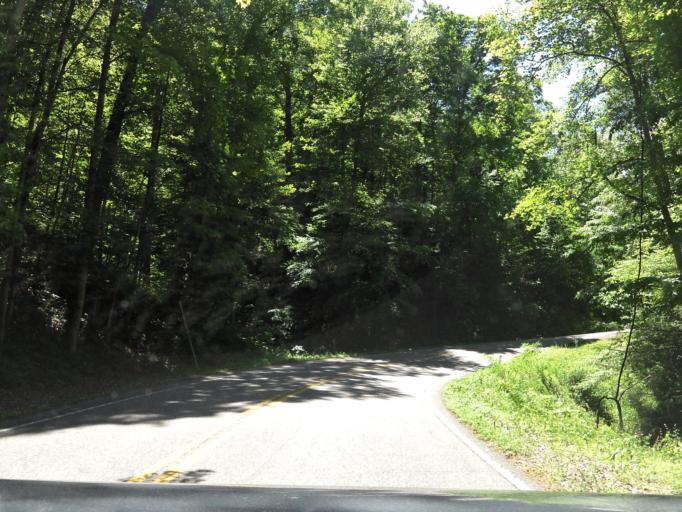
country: US
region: North Carolina
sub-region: Graham County
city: Robbinsville
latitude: 35.4903
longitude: -83.9303
